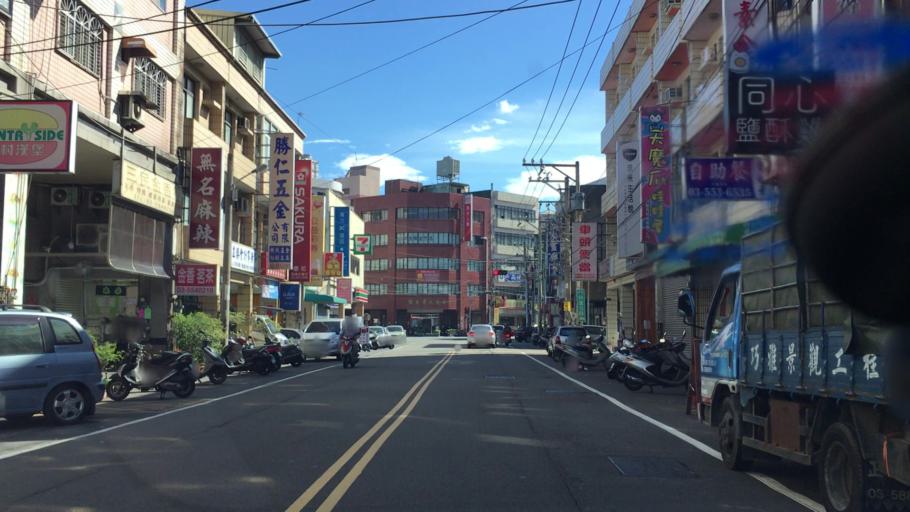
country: TW
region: Taiwan
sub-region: Hsinchu
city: Zhubei
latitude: 24.8344
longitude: 121.0182
